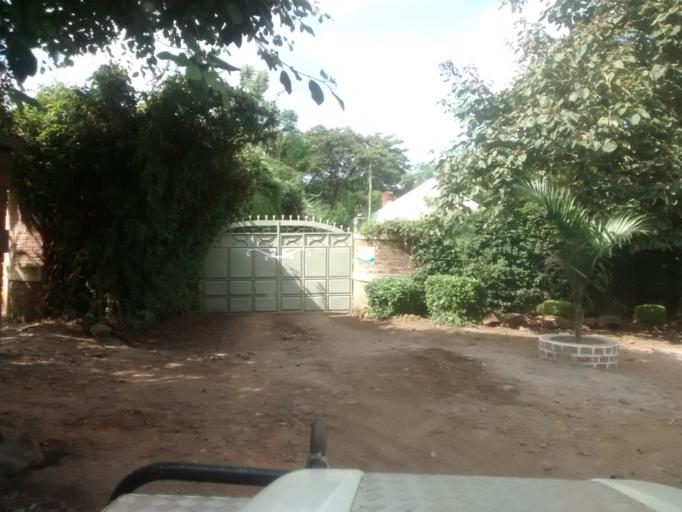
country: TZ
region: Arusha
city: Usa River
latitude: -3.3593
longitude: 36.8400
